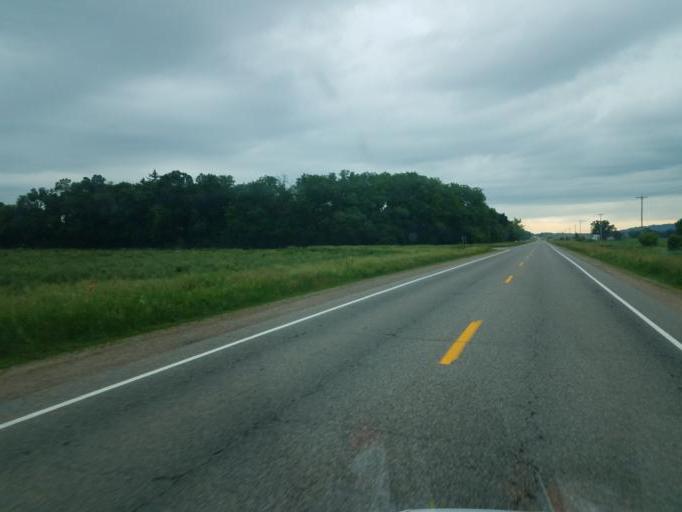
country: US
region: Wisconsin
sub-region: Juneau County
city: Mauston
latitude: 43.7890
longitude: -90.1234
